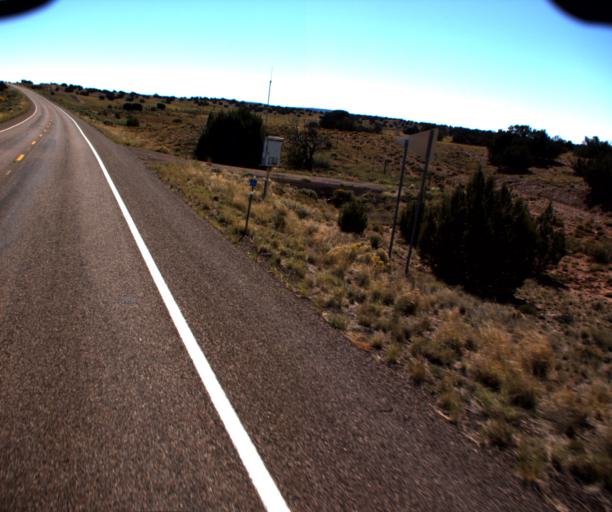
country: US
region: Arizona
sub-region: Apache County
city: Saint Johns
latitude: 34.5977
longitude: -109.6326
